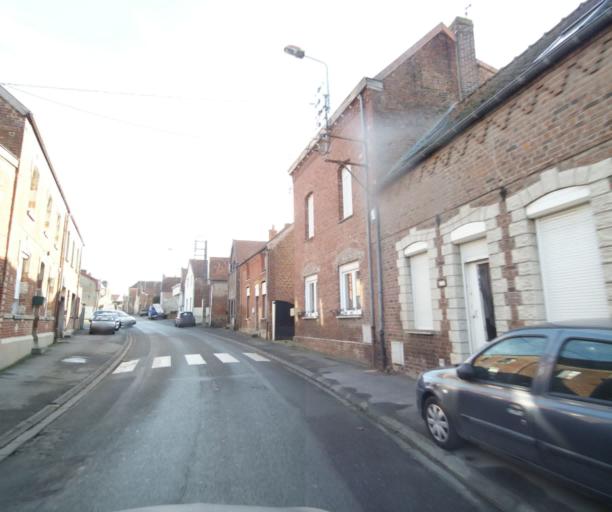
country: FR
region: Nord-Pas-de-Calais
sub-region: Departement du Nord
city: Maing
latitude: 50.3079
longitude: 3.4861
